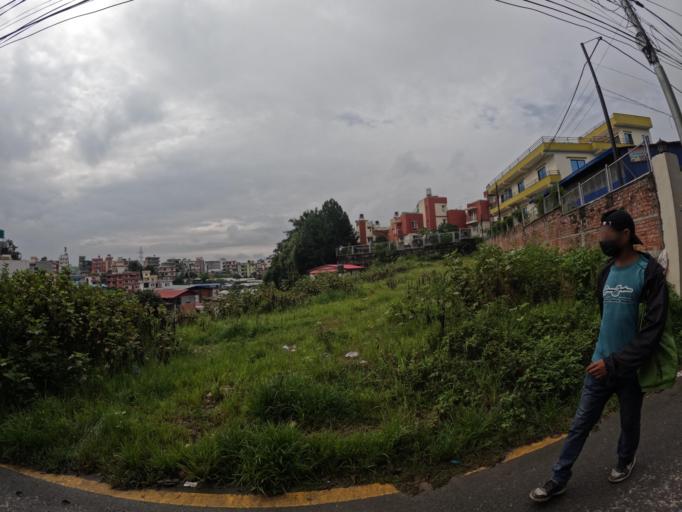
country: NP
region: Central Region
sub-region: Bagmati Zone
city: Kathmandu
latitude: 27.7631
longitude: 85.3277
